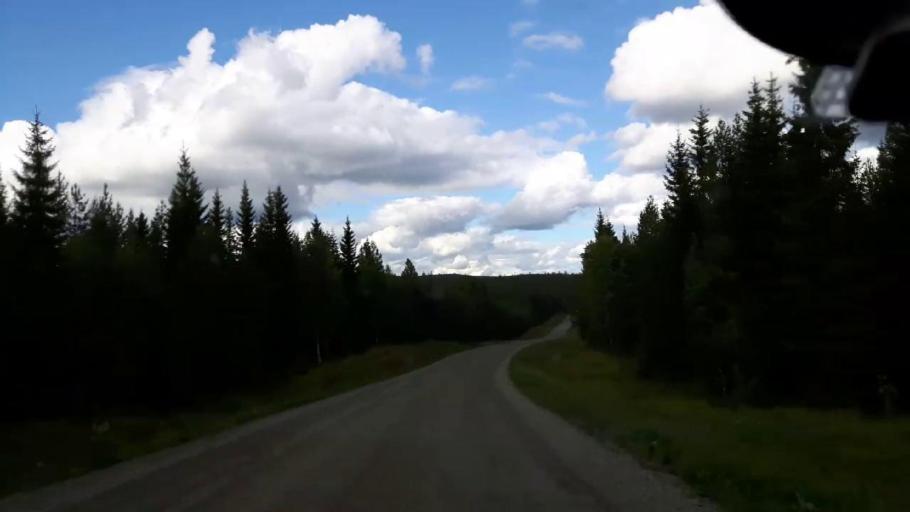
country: SE
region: Jaemtland
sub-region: Stroemsunds Kommun
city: Stroemsund
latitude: 63.4086
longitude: 15.5622
